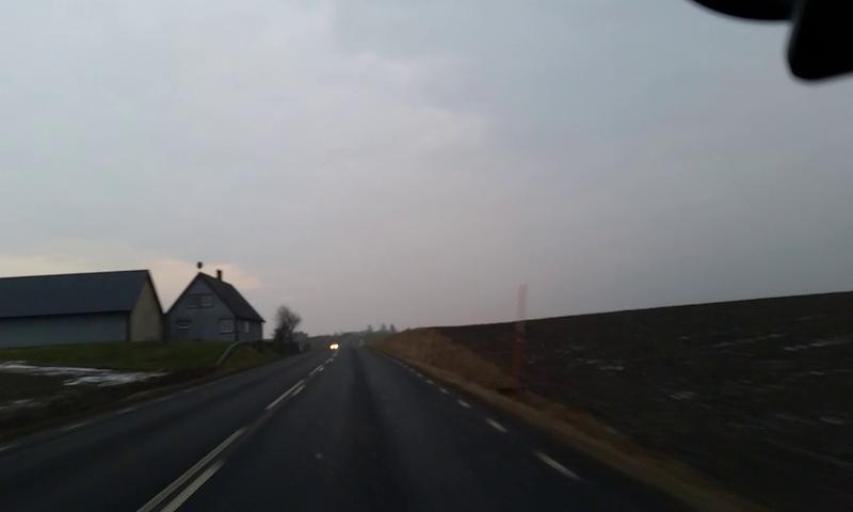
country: SE
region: Skane
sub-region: Angelholms Kommun
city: AEngelholm
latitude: 56.2666
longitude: 12.8888
